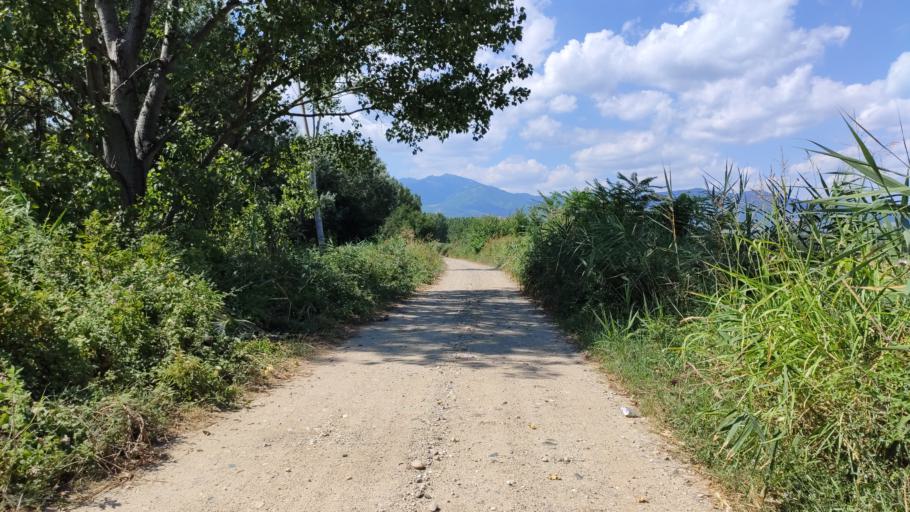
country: GR
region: East Macedonia and Thrace
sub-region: Nomos Rodopis
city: Komotini
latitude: 41.1125
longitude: 25.3706
